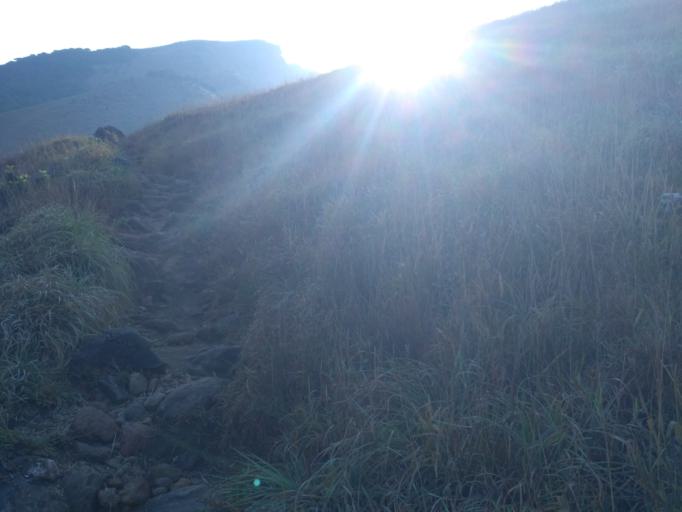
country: IN
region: Karnataka
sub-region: Kodagu
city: Somvarpet
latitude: 12.6643
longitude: 75.6716
